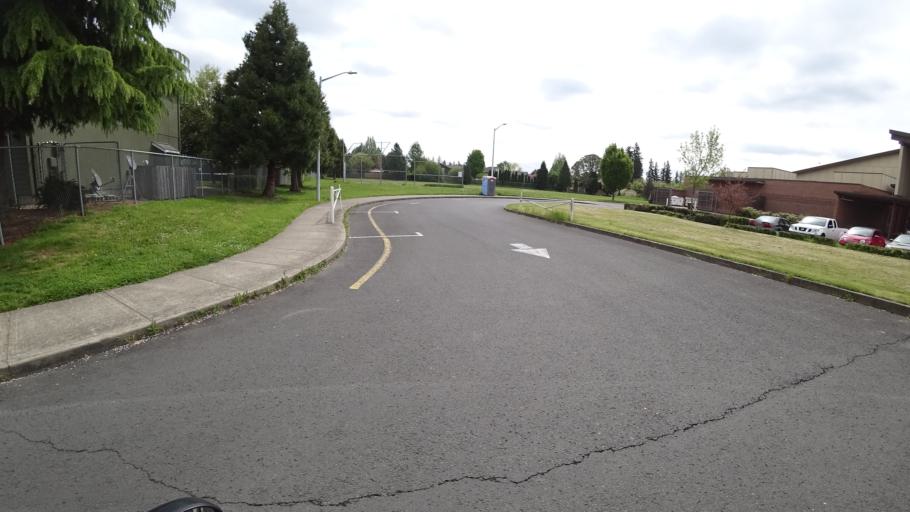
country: US
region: Oregon
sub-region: Washington County
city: Hillsboro
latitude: 45.5470
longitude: -122.9925
